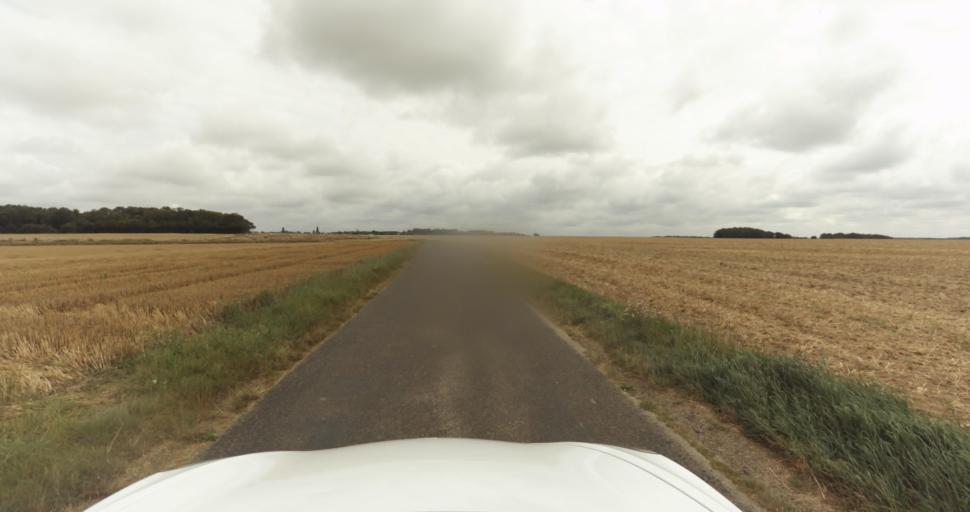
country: FR
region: Haute-Normandie
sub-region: Departement de l'Eure
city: Claville
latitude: 49.0217
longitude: 1.0164
